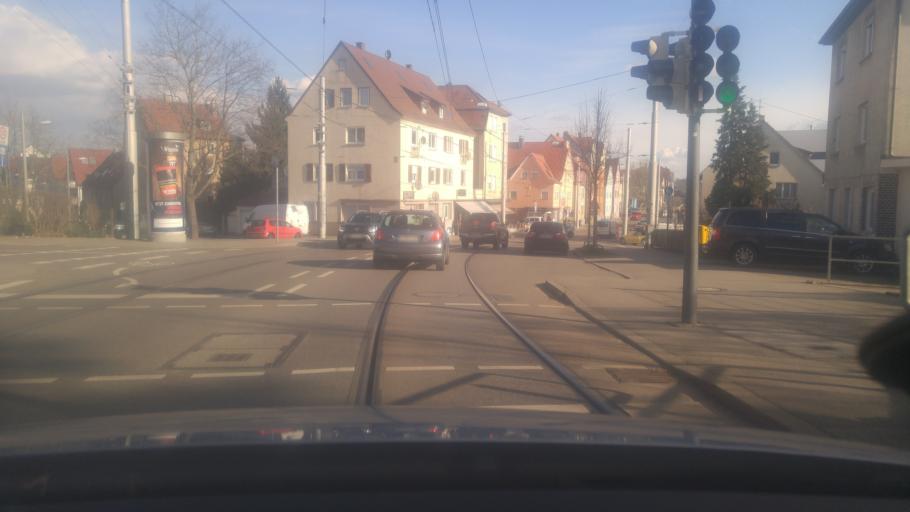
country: DE
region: Baden-Wuerttemberg
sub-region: Regierungsbezirk Stuttgart
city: Stuttgart Feuerbach
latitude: 48.8382
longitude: 9.1611
